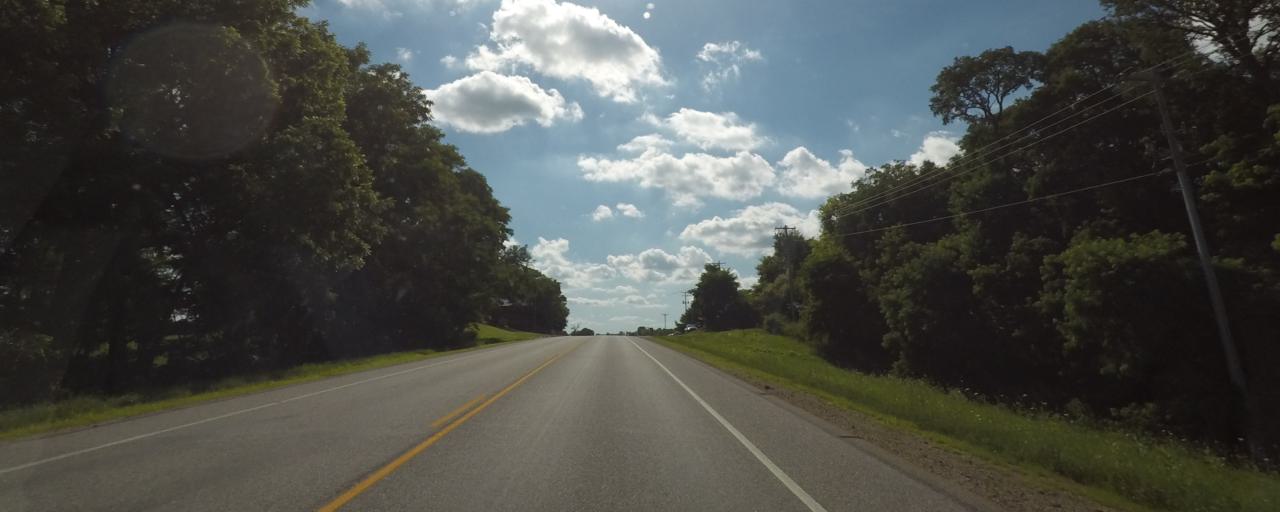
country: US
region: Wisconsin
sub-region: Rock County
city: Edgerton
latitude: 42.9202
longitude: -89.1054
